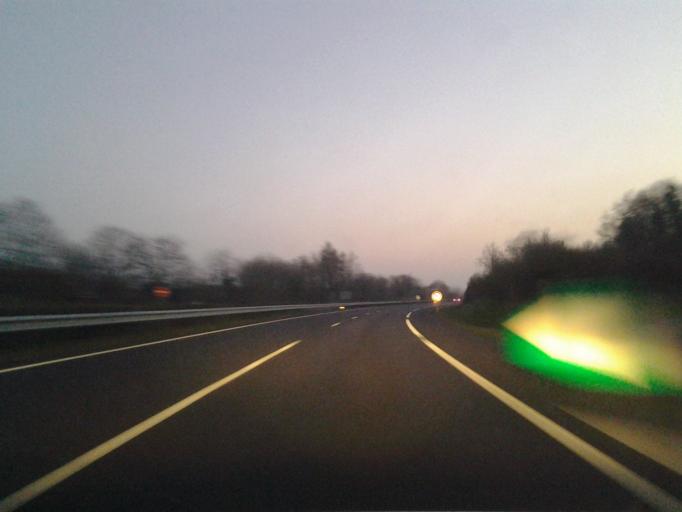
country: FR
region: Pays de la Loire
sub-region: Departement de la Vendee
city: Challans
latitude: 46.8512
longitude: -1.8506
